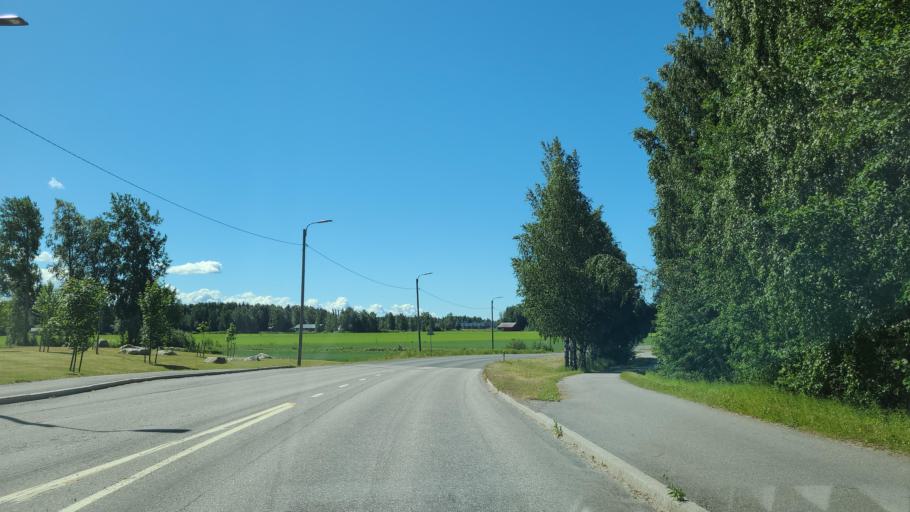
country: FI
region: Ostrobothnia
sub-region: Vaasa
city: Ristinummi
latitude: 63.0568
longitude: 21.7308
